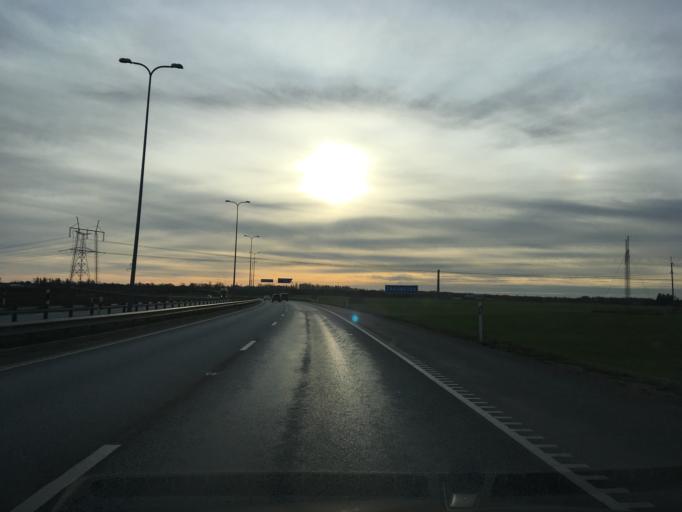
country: EE
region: Ida-Virumaa
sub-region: Kohtla-Jaerve linn
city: Kohtla-Jarve
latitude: 59.3916
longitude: 27.3377
